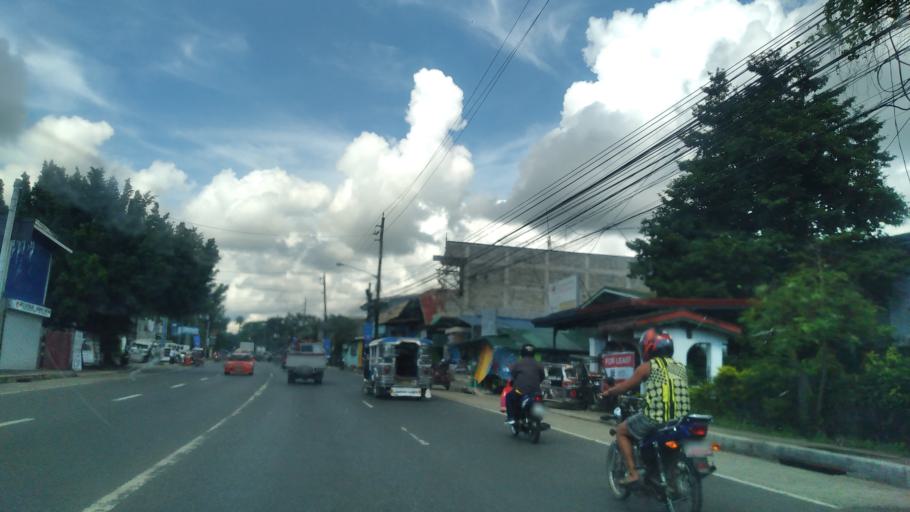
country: PH
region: Calabarzon
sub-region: Province of Quezon
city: Isabang
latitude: 13.9448
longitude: 121.5915
